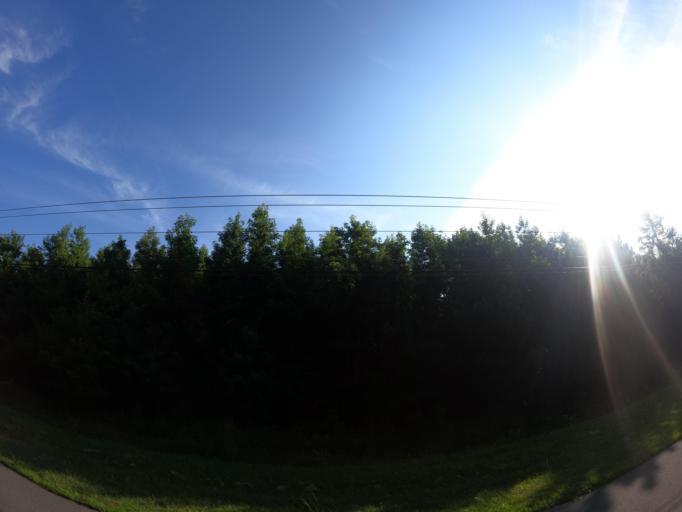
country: US
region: Delaware
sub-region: Sussex County
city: Millsboro
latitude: 38.5614
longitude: -75.2673
